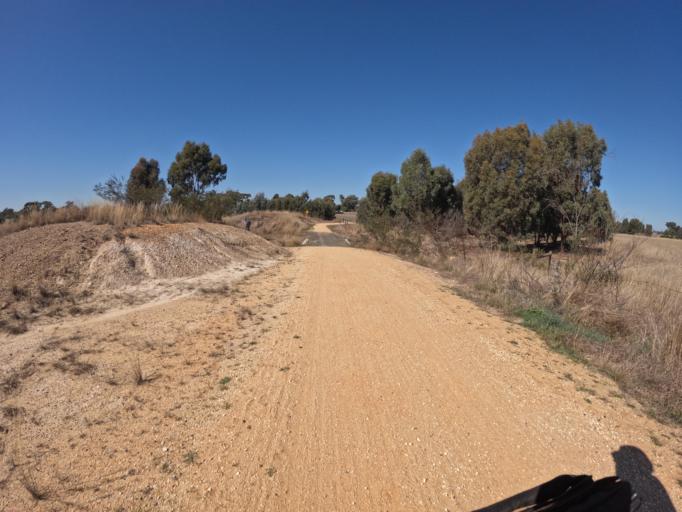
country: AU
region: Victoria
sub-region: Greater Bendigo
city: Kennington
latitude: -36.8236
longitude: 144.5813
